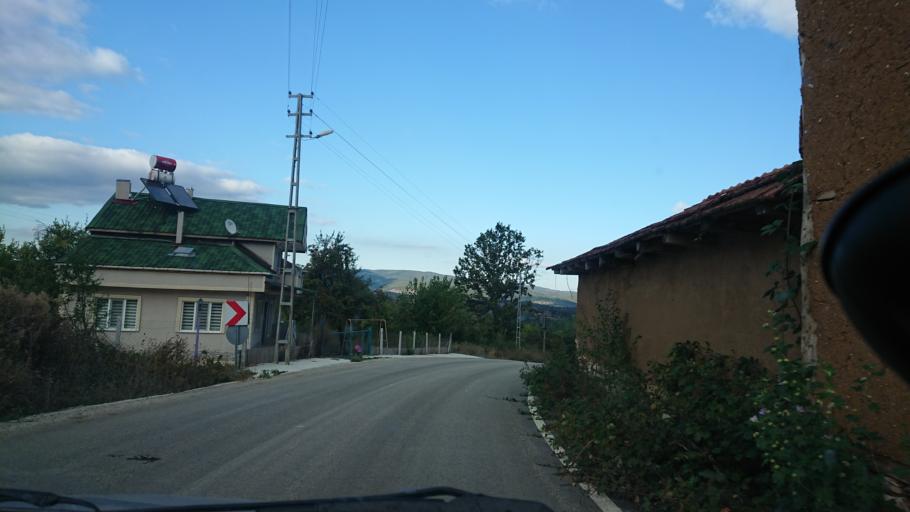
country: TR
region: Bilecik
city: Pazaryeri
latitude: 40.0114
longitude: 29.8004
